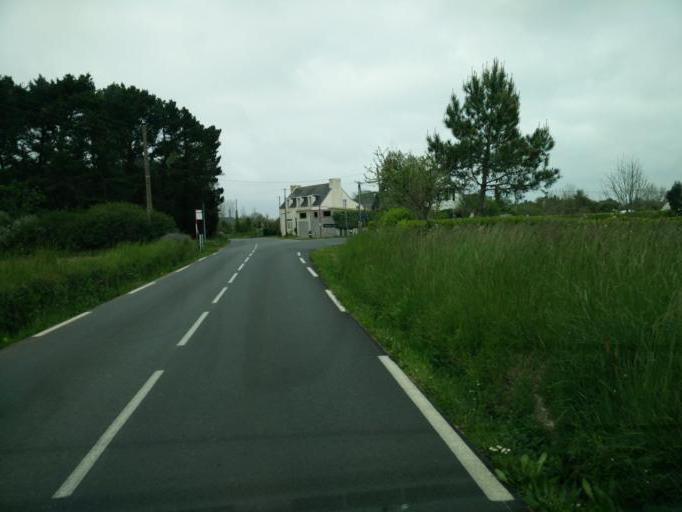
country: FR
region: Brittany
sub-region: Departement du Finistere
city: Loctudy
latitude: 47.8194
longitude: -4.1730
